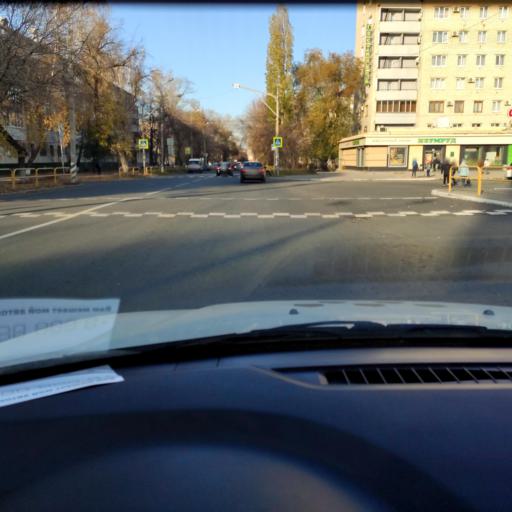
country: RU
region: Samara
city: Tol'yatti
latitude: 53.5157
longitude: 49.4242
